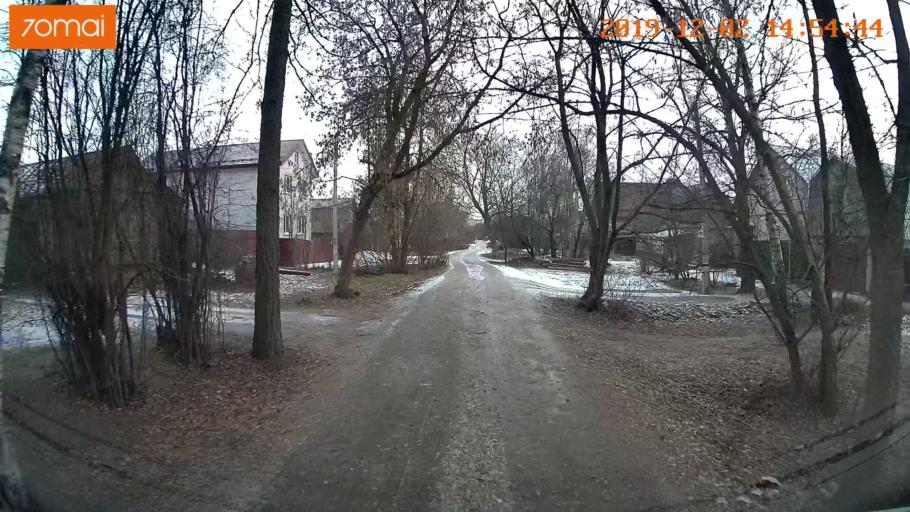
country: RU
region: Ivanovo
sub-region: Gorod Ivanovo
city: Ivanovo
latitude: 56.9748
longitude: 41.0159
